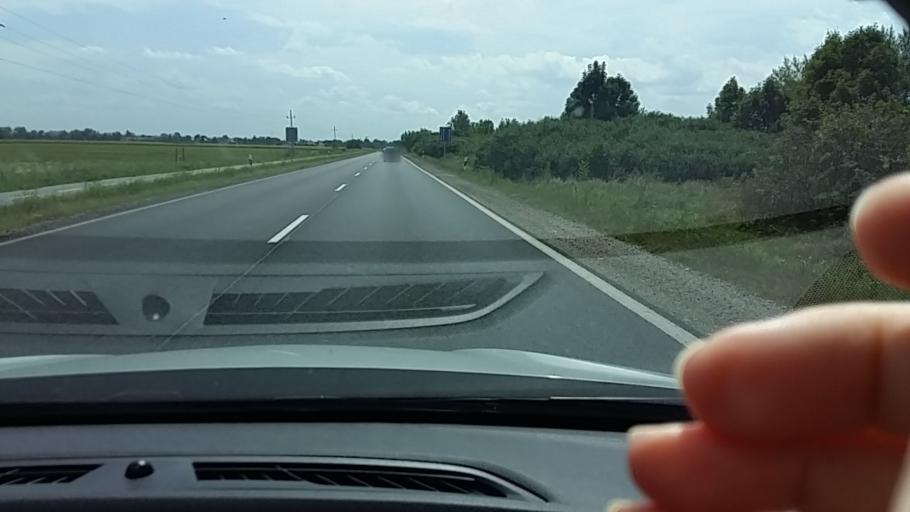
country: HU
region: Borsod-Abauj-Zemplen
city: Malyi
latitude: 48.0069
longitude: 20.8280
